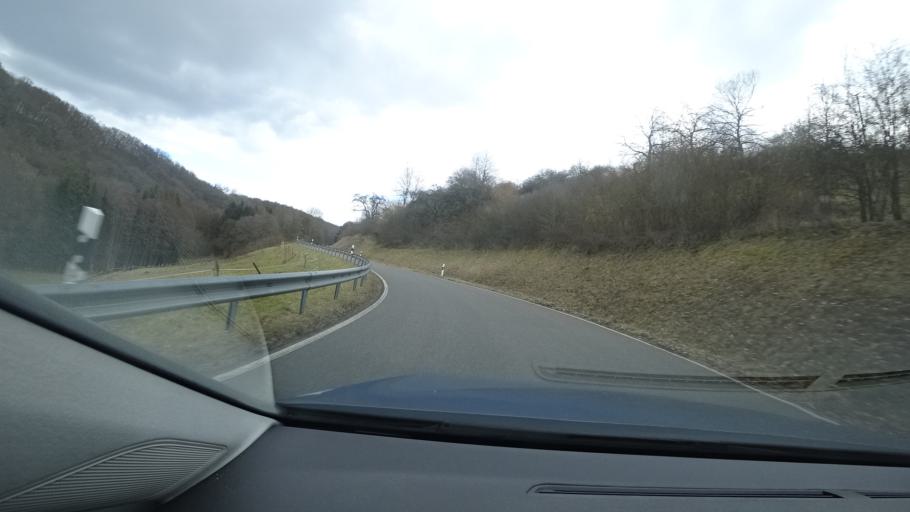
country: DE
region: Rheinland-Pfalz
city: Reichenberg
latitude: 50.1539
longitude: 7.7643
